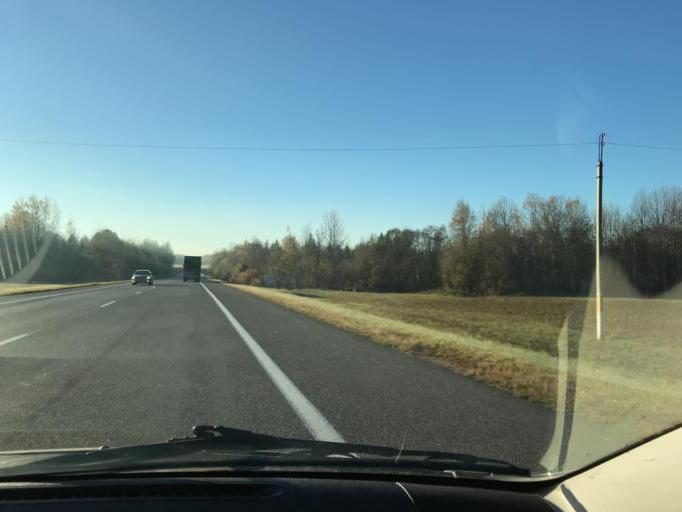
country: BY
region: Vitebsk
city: Vitebsk
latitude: 54.9957
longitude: 30.3391
